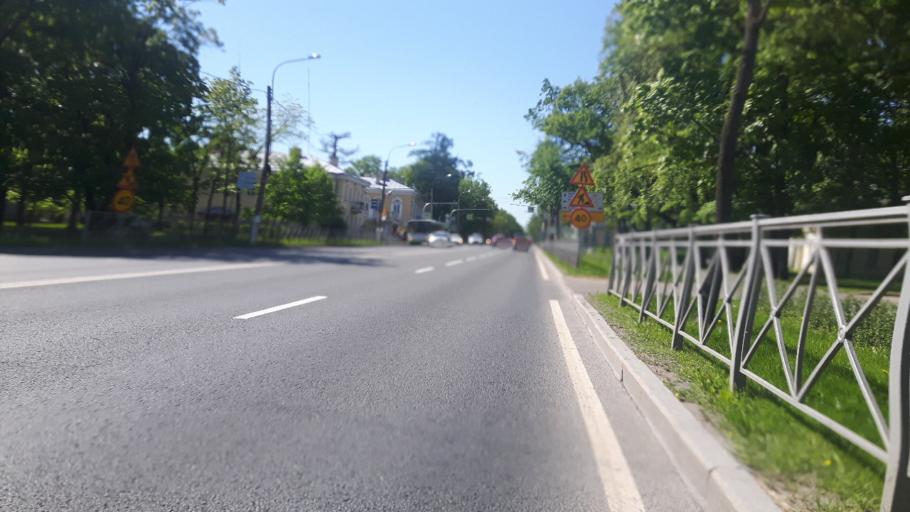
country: RU
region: St.-Petersburg
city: Peterhof
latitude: 59.8778
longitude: 29.9254
